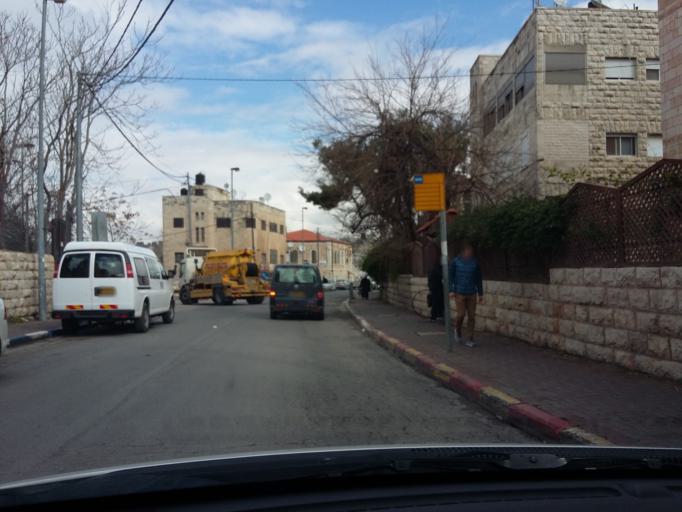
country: PS
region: West Bank
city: East Jerusalem
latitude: 31.7880
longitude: 35.2321
